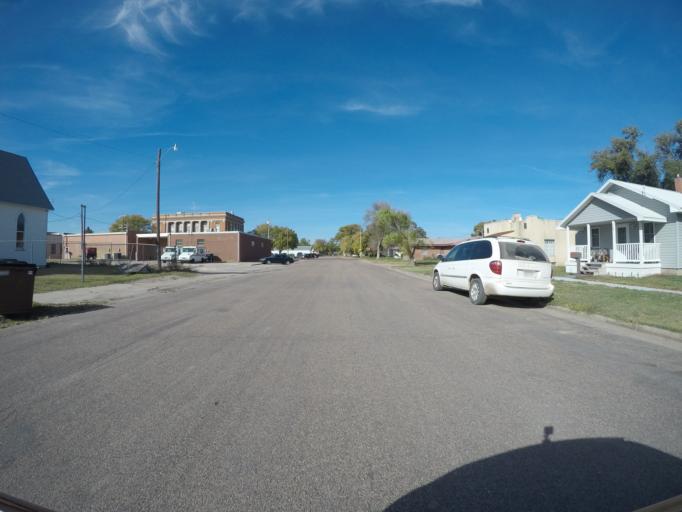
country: US
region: Kansas
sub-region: Decatur County
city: Oberlin
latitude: 39.8183
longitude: -100.5278
